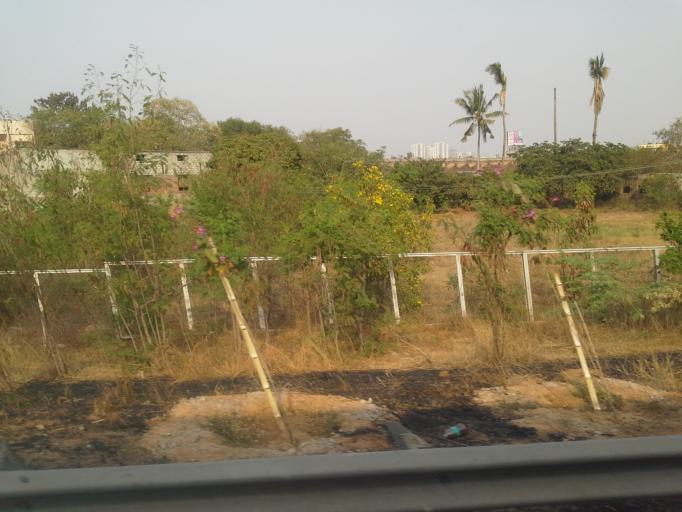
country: IN
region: Telangana
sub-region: Hyderabad
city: Hyderabad
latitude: 17.3937
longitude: 78.3504
